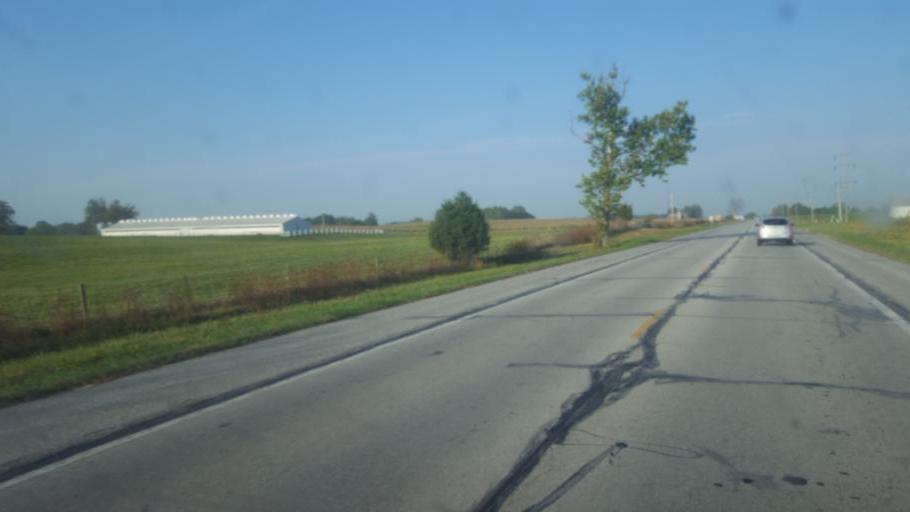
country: US
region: Indiana
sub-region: LaGrange County
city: Lagrange
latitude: 41.6410
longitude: -85.4804
